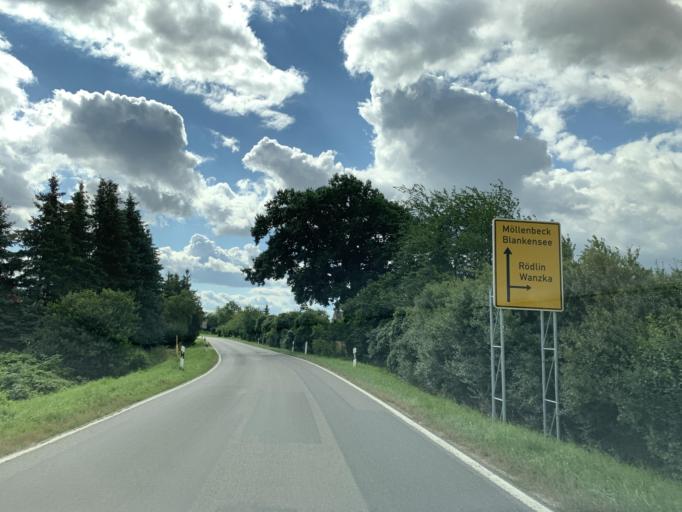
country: DE
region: Mecklenburg-Vorpommern
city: Blankensee
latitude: 53.4134
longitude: 13.2242
